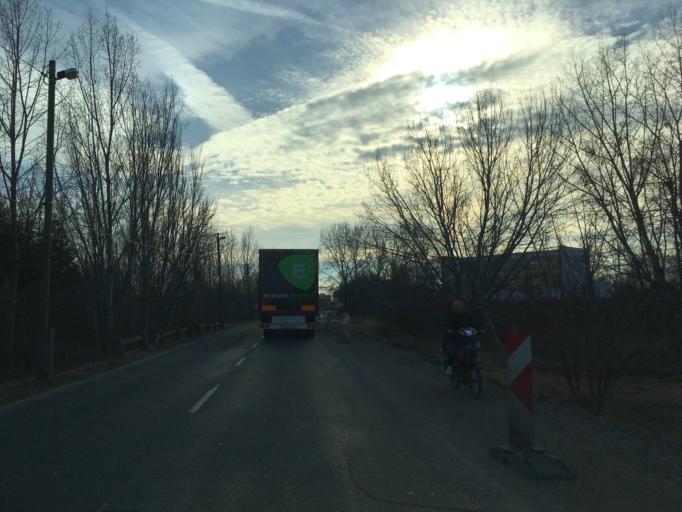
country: HU
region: Gyor-Moson-Sopron
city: Gyor
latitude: 47.6986
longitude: 17.6626
